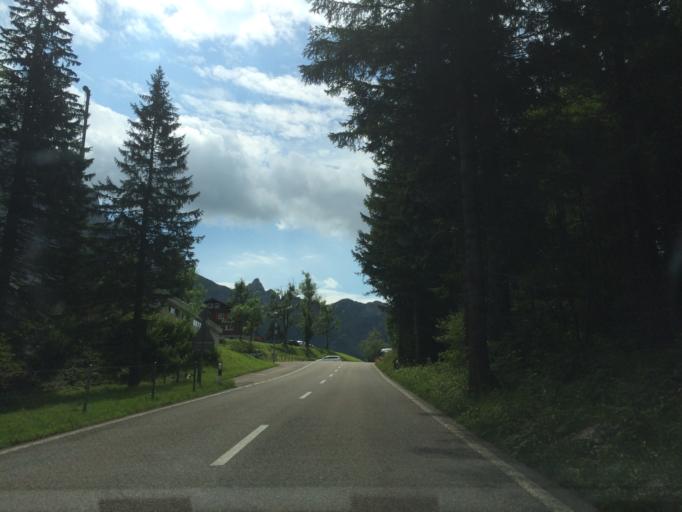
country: CH
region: Appenzell Ausserrhoden
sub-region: Bezirk Hinterland
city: Urnasch
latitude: 47.2573
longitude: 9.3090
